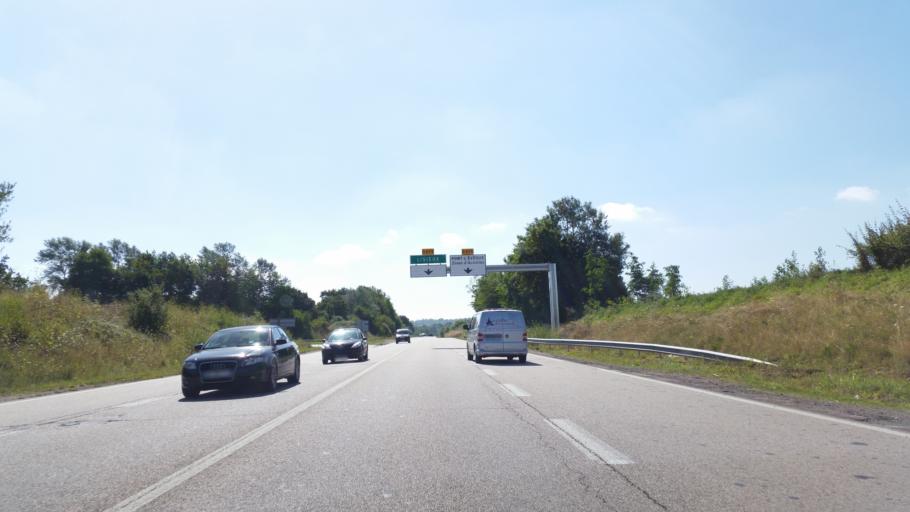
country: FR
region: Lower Normandy
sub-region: Departement du Calvados
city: Saint-Gatien-des-Bois
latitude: 49.2869
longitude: 0.2072
